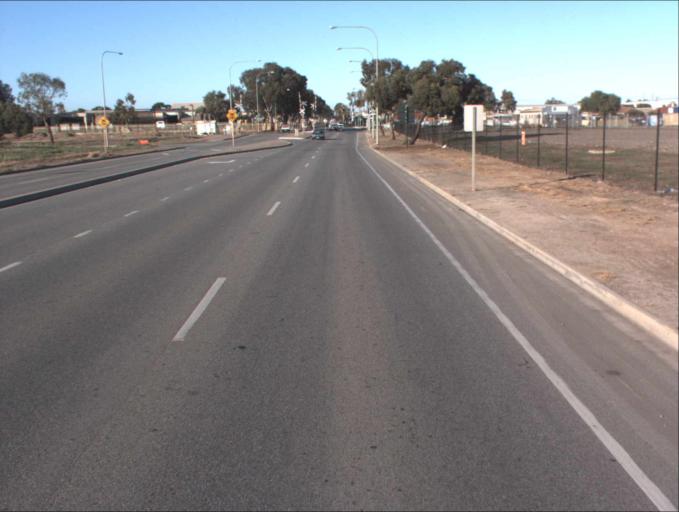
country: AU
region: South Australia
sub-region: Port Adelaide Enfield
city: Alberton
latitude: -34.8386
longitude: 138.5459
